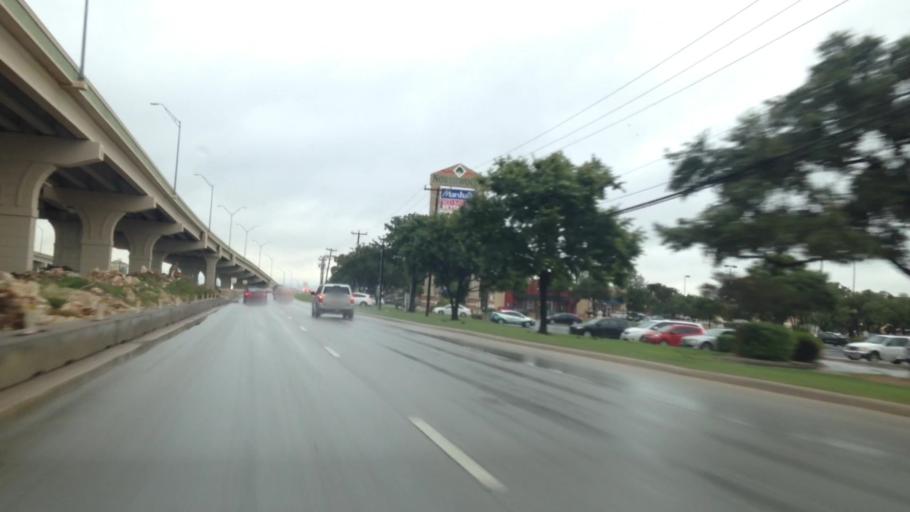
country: US
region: Texas
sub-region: Bexar County
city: Hollywood Park
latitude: 29.6081
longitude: -98.4657
